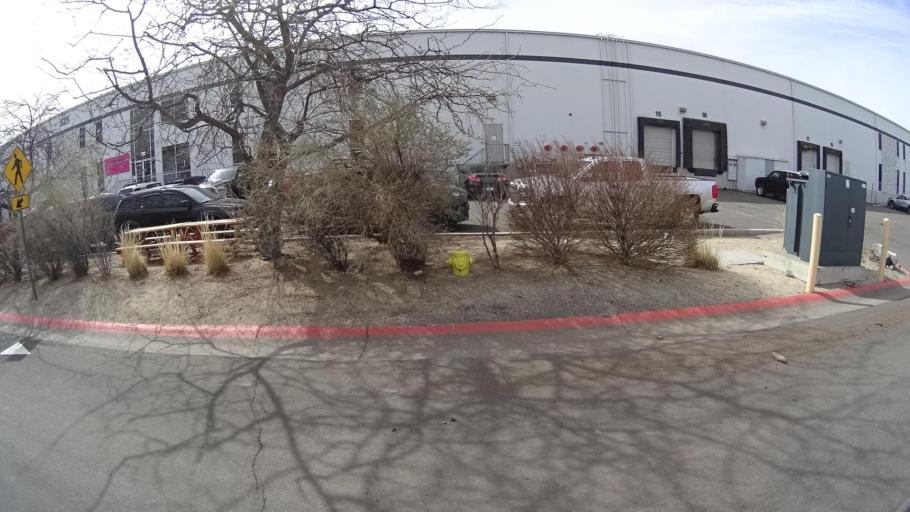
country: US
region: Nevada
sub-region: Washoe County
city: Sparks
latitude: 39.5190
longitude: -119.7510
